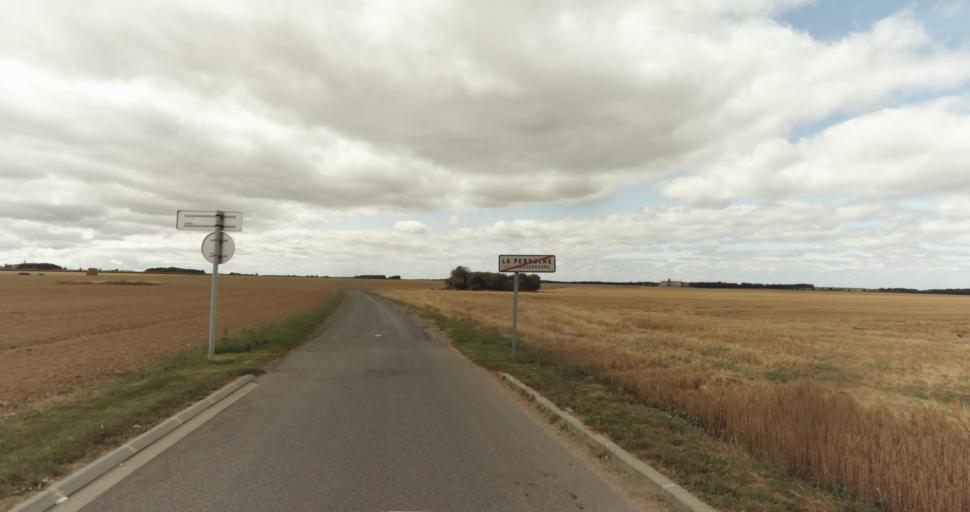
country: FR
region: Haute-Normandie
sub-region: Departement de l'Eure
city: Evreux
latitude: 48.9221
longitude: 1.1839
